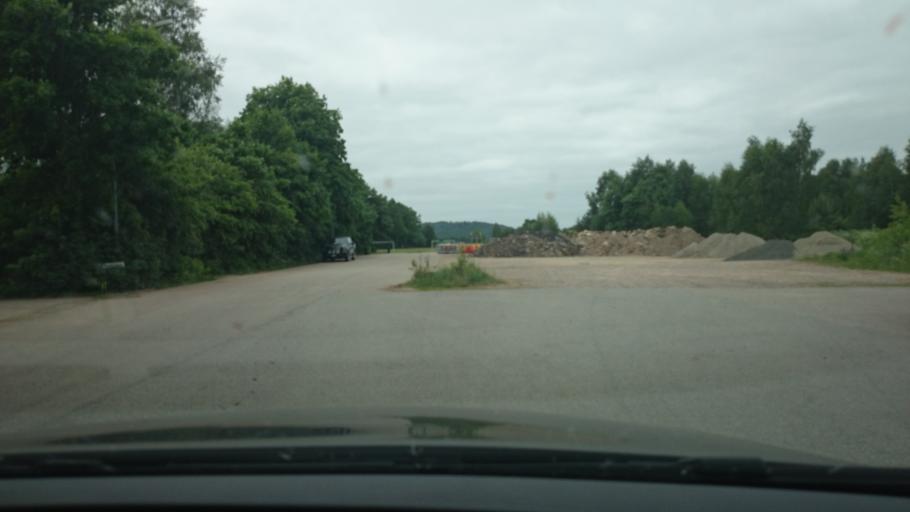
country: SE
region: Halland
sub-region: Hylte Kommun
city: Torup
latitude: 56.9581
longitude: 13.1314
